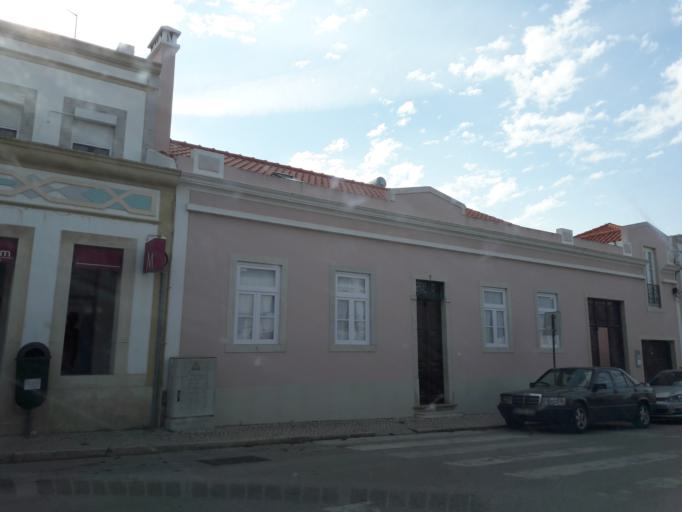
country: PT
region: Leiria
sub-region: Peniche
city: Atouguia da Baleia
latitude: 39.3367
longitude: -9.3259
